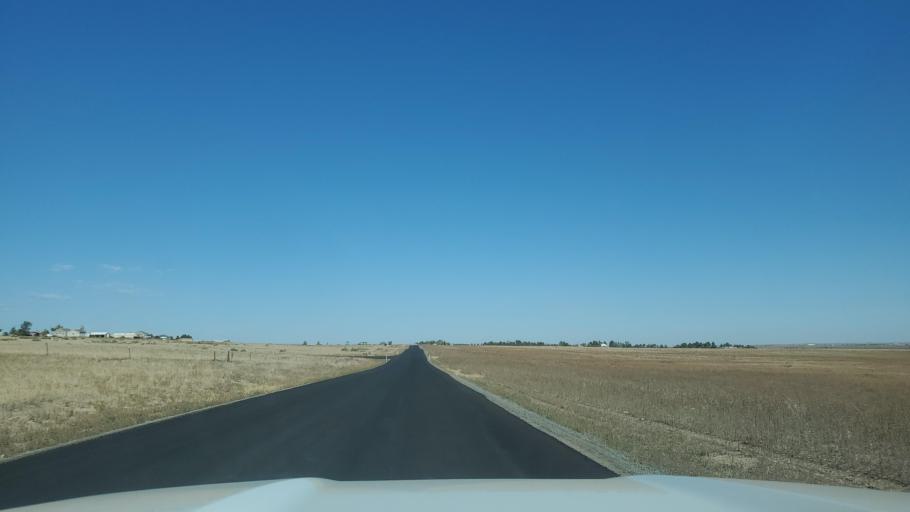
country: US
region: Colorado
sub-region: Adams County
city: Bennett
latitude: 39.7583
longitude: -104.3771
